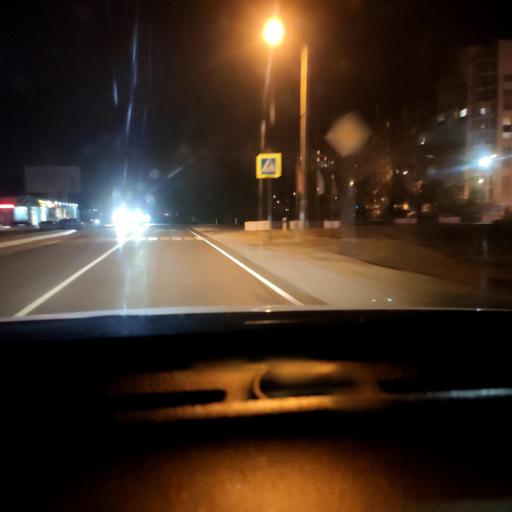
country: RU
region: Voronezj
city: Novaya Usman'
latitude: 51.6704
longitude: 39.4059
